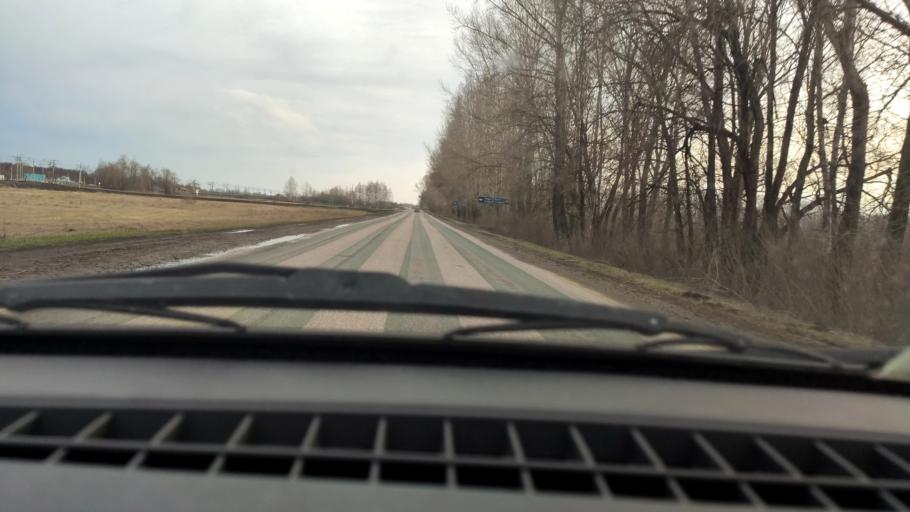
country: RU
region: Bashkortostan
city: Chishmy
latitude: 54.4530
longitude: 55.2499
